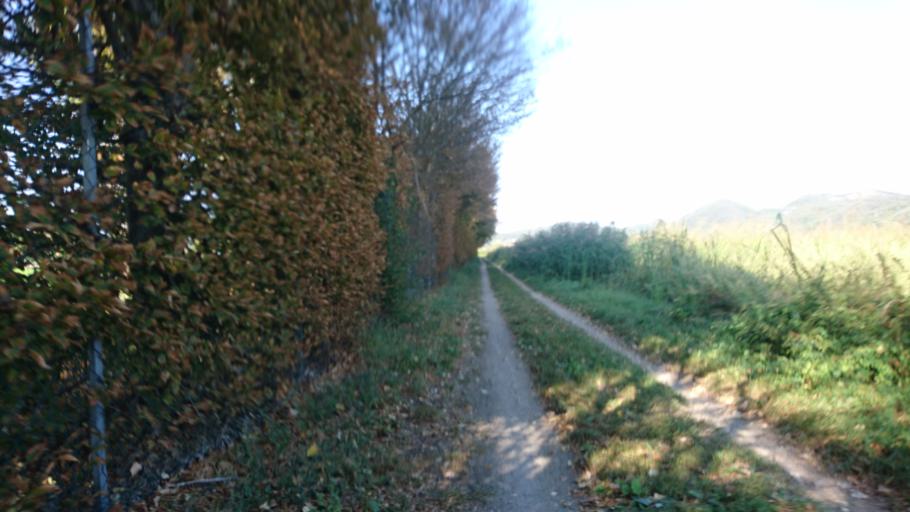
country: IT
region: Veneto
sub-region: Provincia di Padova
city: Galzignano
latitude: 45.2921
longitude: 11.7474
